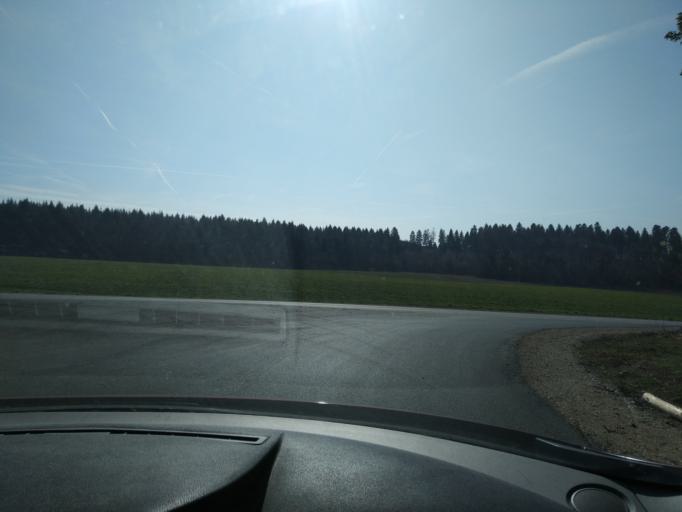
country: FR
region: Franche-Comte
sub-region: Departement du Doubs
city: Saone
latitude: 47.2314
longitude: 6.1371
